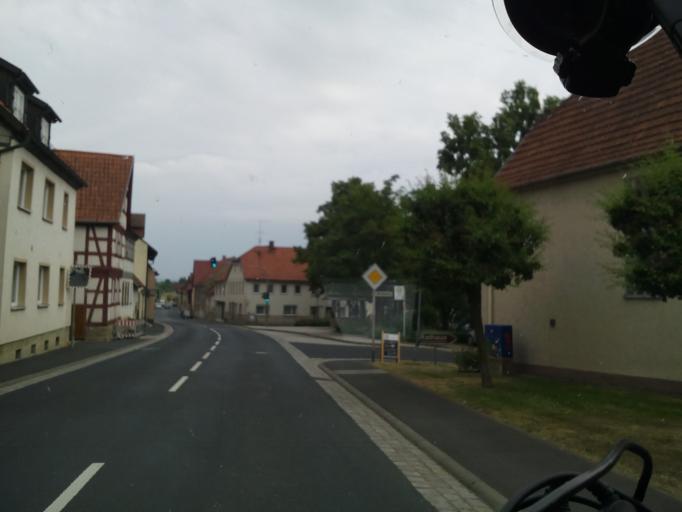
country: DE
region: Bavaria
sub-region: Regierungsbezirk Unterfranken
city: Stockheim
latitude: 50.4588
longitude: 10.2713
